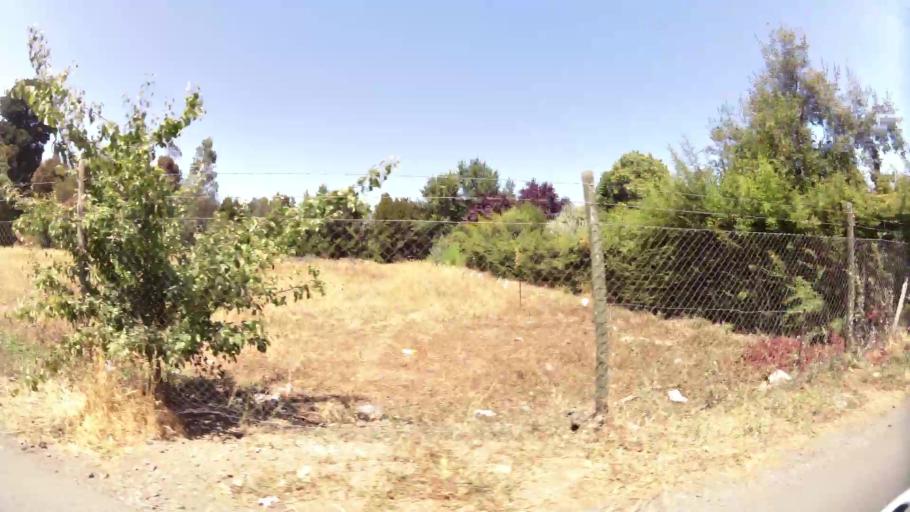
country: CL
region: Maule
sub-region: Provincia de Curico
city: Curico
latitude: -34.9934
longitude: -71.2077
